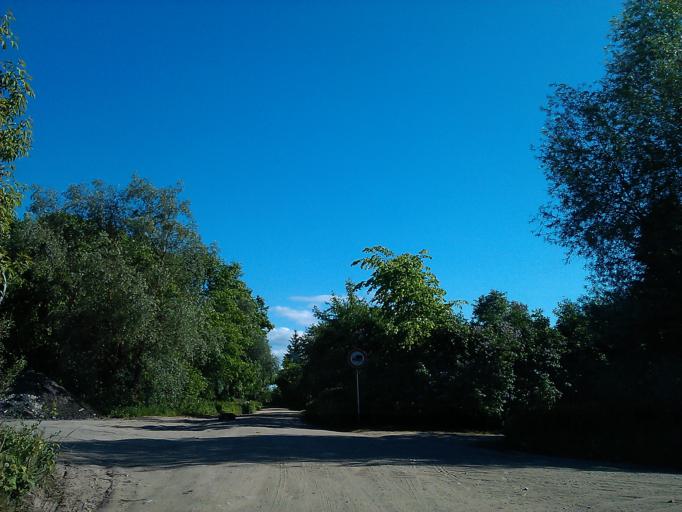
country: LV
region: Adazi
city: Adazi
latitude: 57.0878
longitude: 24.3209
